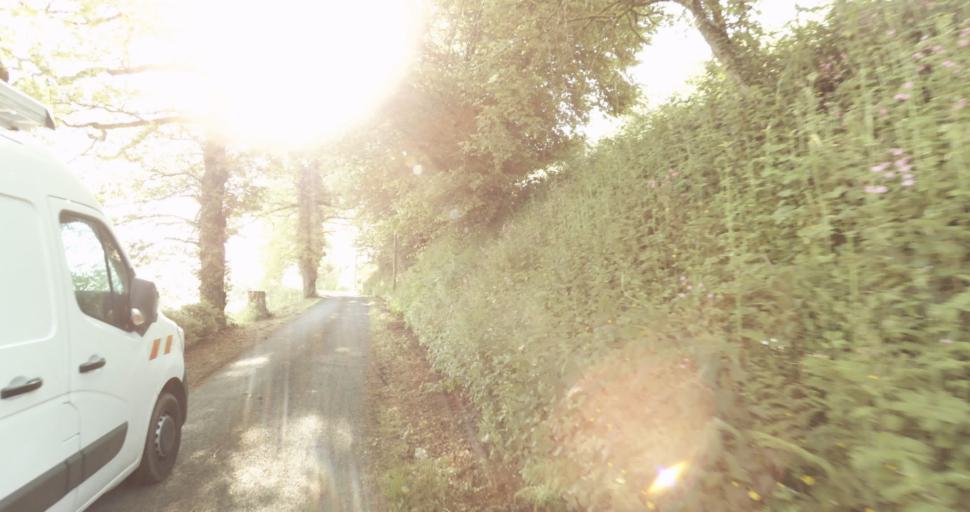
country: FR
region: Limousin
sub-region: Departement de la Haute-Vienne
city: Le Vigen
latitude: 45.7466
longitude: 1.2907
